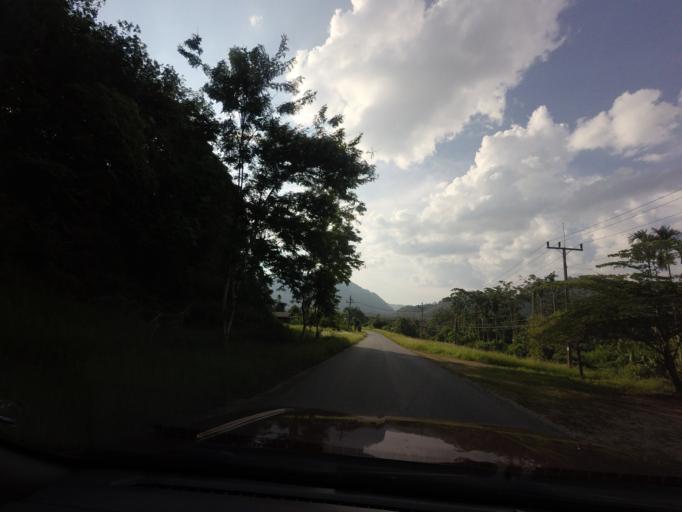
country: TH
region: Yala
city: Ban Nang Sata
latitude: 6.2200
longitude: 101.2302
